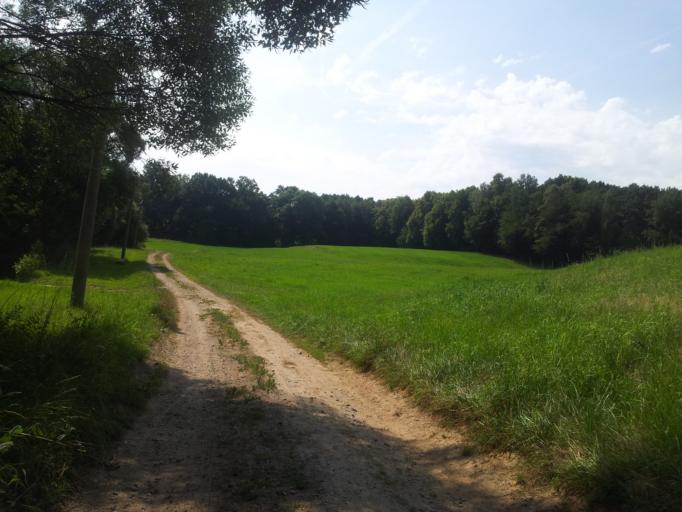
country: DE
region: Saxony
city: Panschwitz-Kuckau
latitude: 51.2145
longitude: 14.1956
